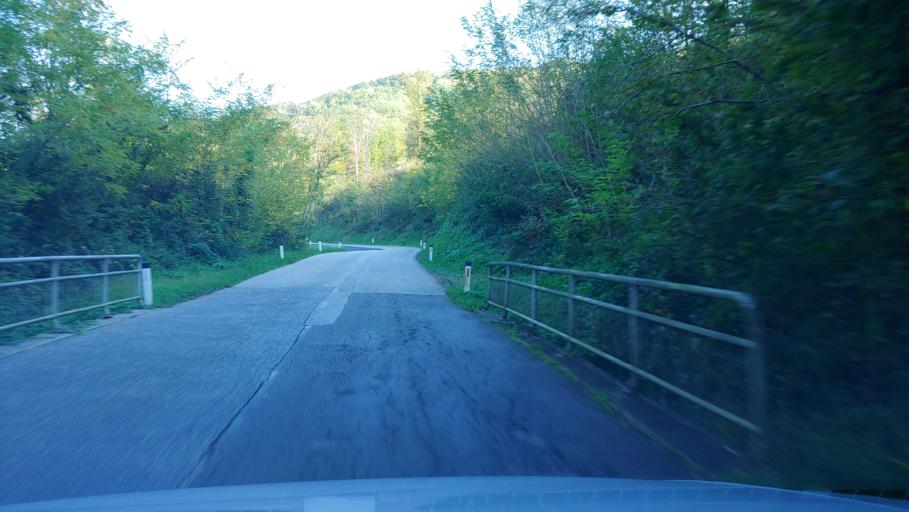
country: SI
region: Vipava
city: Vipava
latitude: 45.8124
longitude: 13.9098
